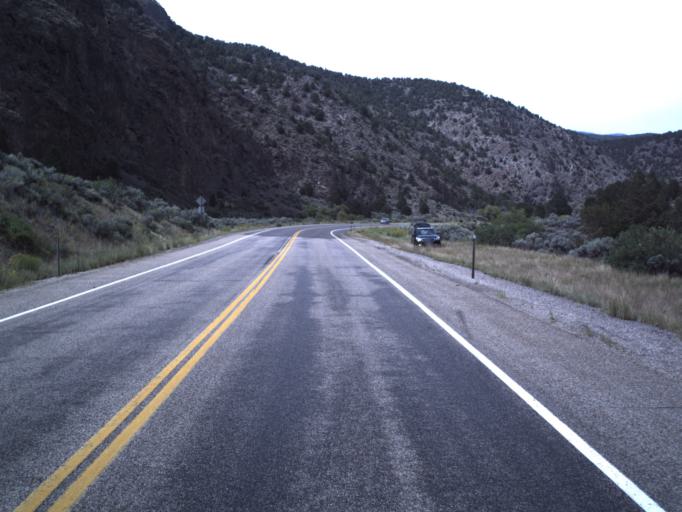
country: US
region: Utah
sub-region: Piute County
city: Junction
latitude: 38.1091
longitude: -112.3366
